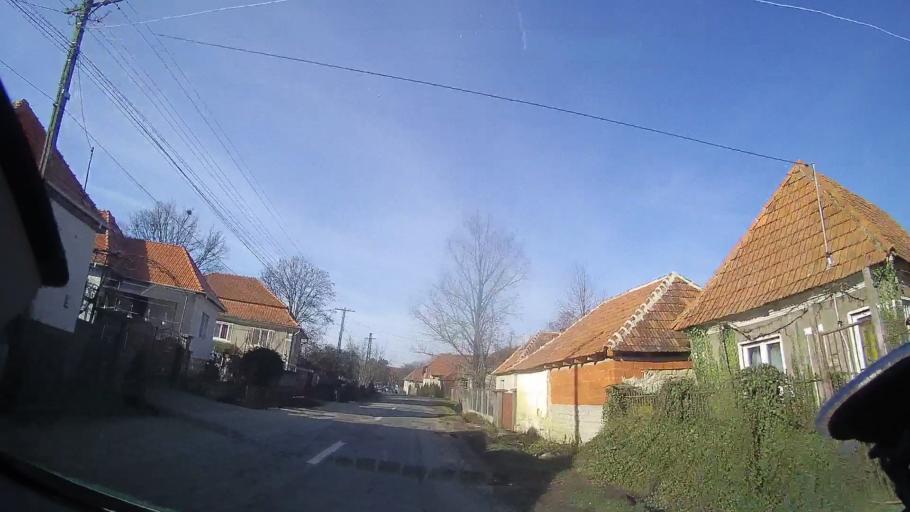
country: RO
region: Bihor
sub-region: Comuna Magesti
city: Magesti
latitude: 47.0108
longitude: 22.4472
